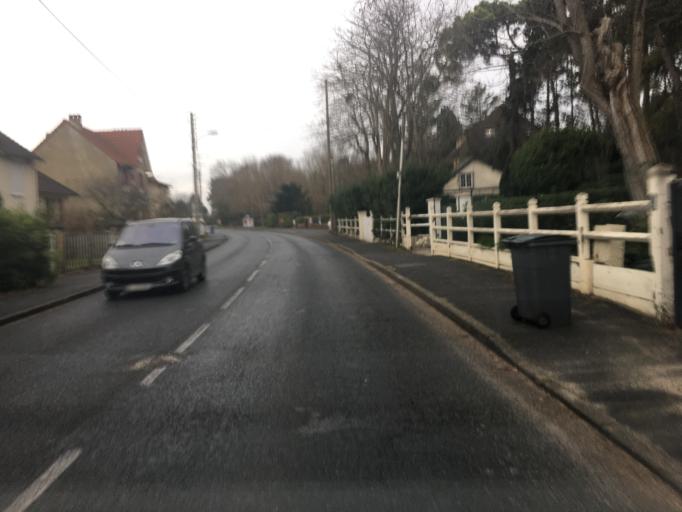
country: FR
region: Lower Normandy
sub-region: Departement du Calvados
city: Merville-Franceville-Plage
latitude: 49.2786
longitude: -0.2045
